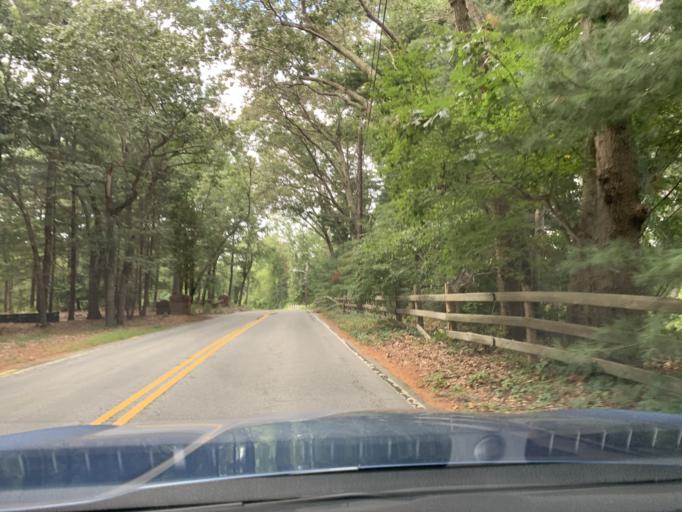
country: US
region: Rhode Island
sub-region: Kent County
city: East Greenwich
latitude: 41.6209
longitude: -71.4453
